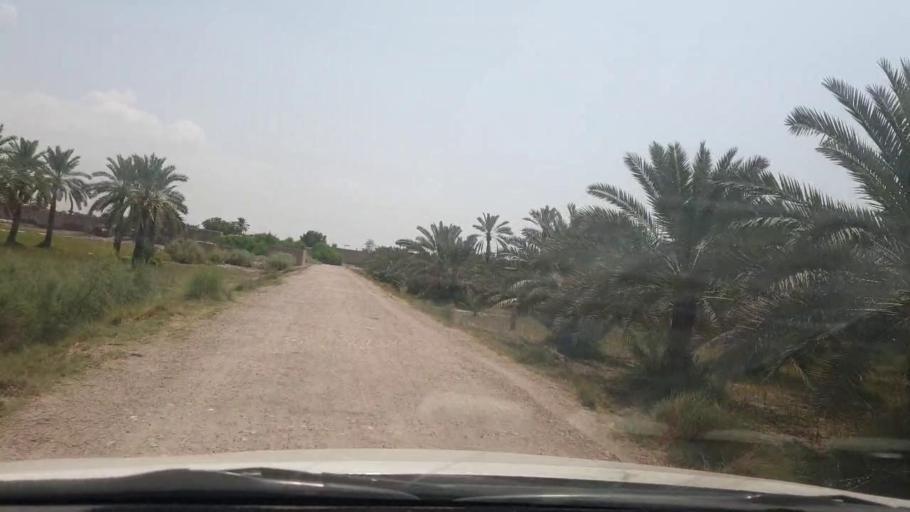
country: PK
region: Sindh
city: Khairpur
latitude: 27.5601
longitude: 68.8294
